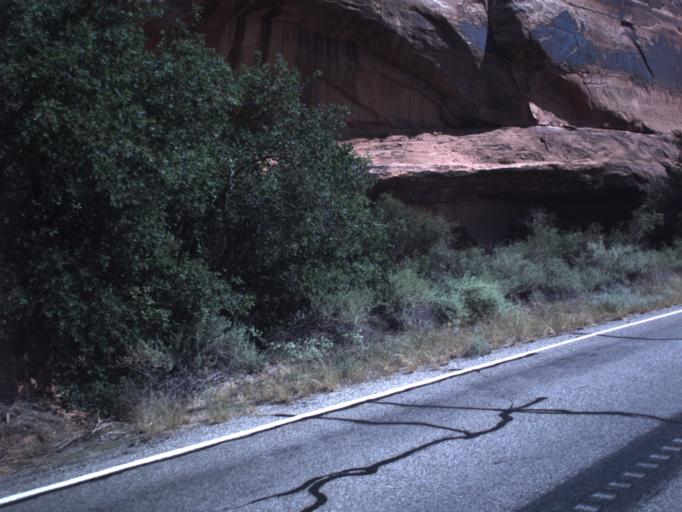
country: US
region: Utah
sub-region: Grand County
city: Moab
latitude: 38.5619
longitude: -109.6314
